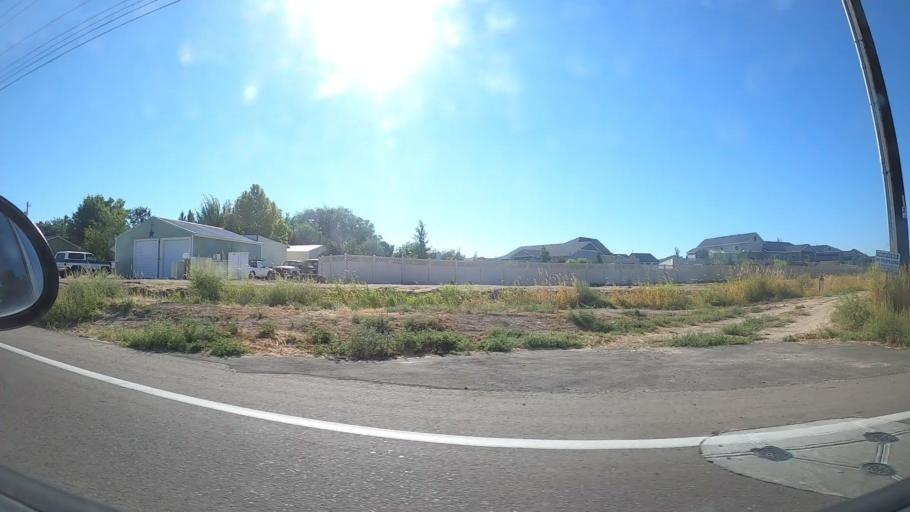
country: US
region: Idaho
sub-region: Canyon County
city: Nampa
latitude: 43.5605
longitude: -116.6129
